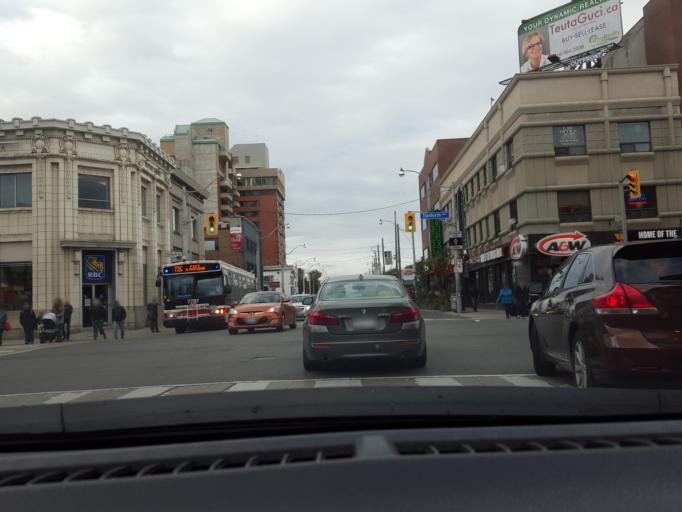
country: CA
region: Ontario
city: Toronto
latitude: 43.6787
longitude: -79.3448
